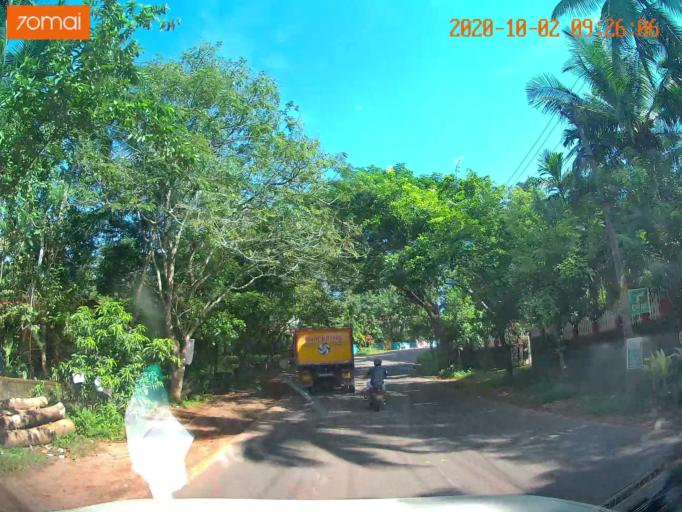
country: IN
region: Kerala
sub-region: Kozhikode
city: Naduvannur
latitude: 11.5908
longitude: 75.7668
